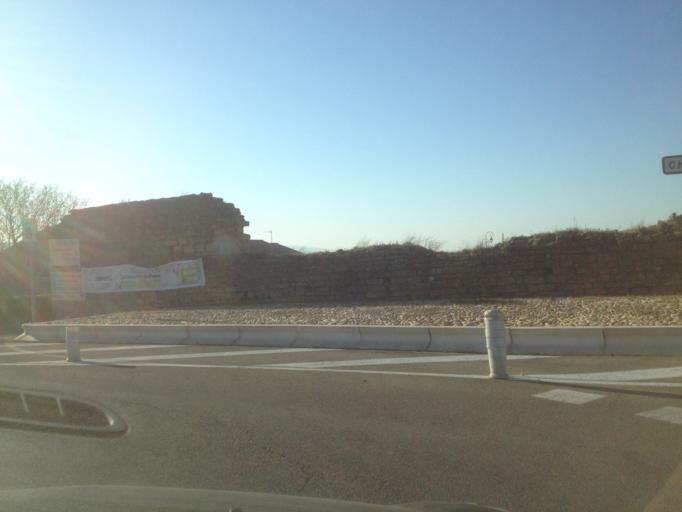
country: FR
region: Provence-Alpes-Cote d'Azur
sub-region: Departement du Vaucluse
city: Chateauneuf-du-Pape
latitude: 44.0616
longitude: 4.8285
